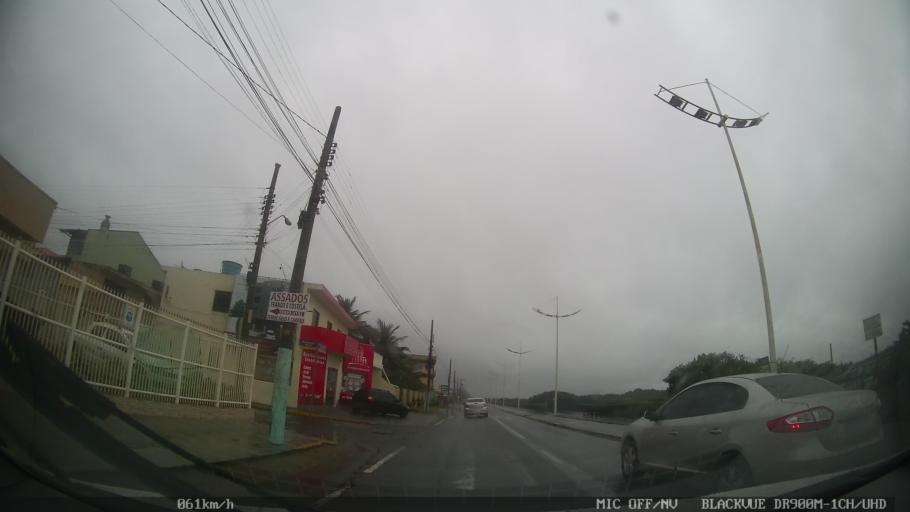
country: BR
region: Santa Catarina
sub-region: Navegantes
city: Navegantes
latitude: -26.8922
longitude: -48.6427
